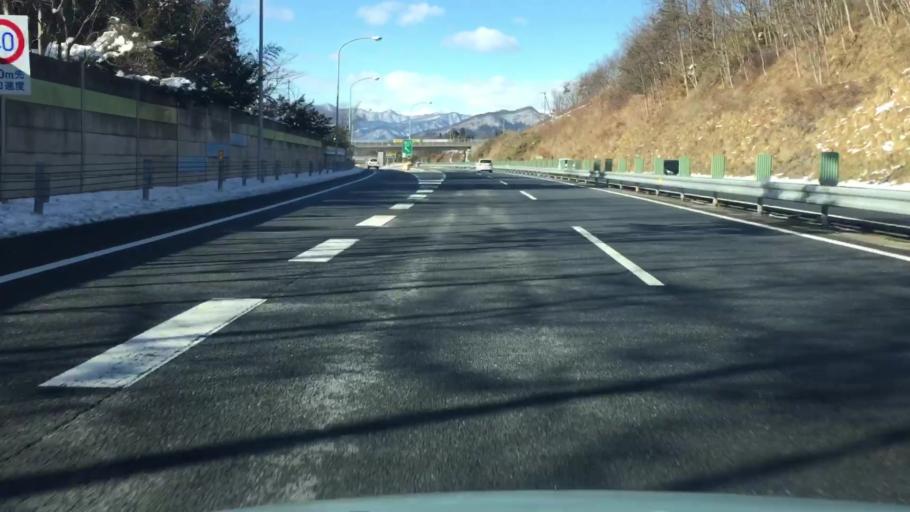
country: JP
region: Gunma
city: Numata
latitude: 36.6755
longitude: 139.0258
